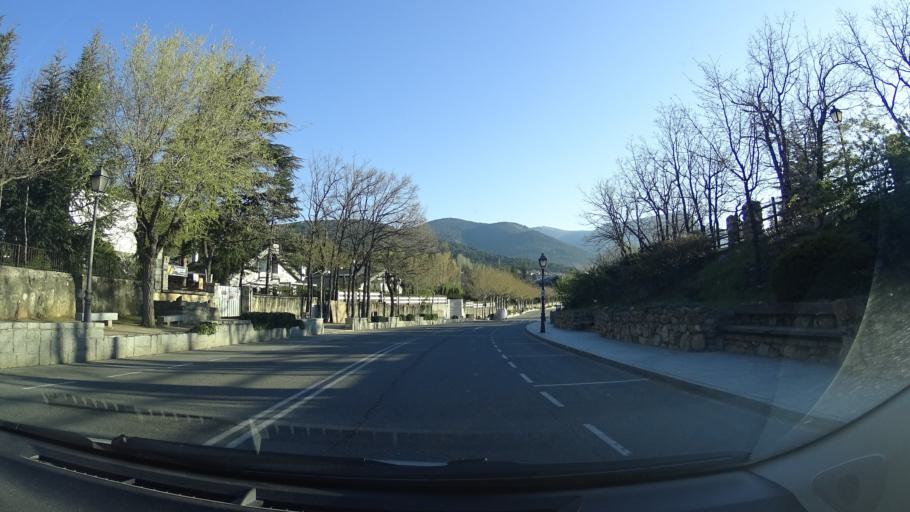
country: ES
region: Madrid
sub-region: Provincia de Madrid
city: Navacerrada
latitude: 40.7257
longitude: -4.0193
